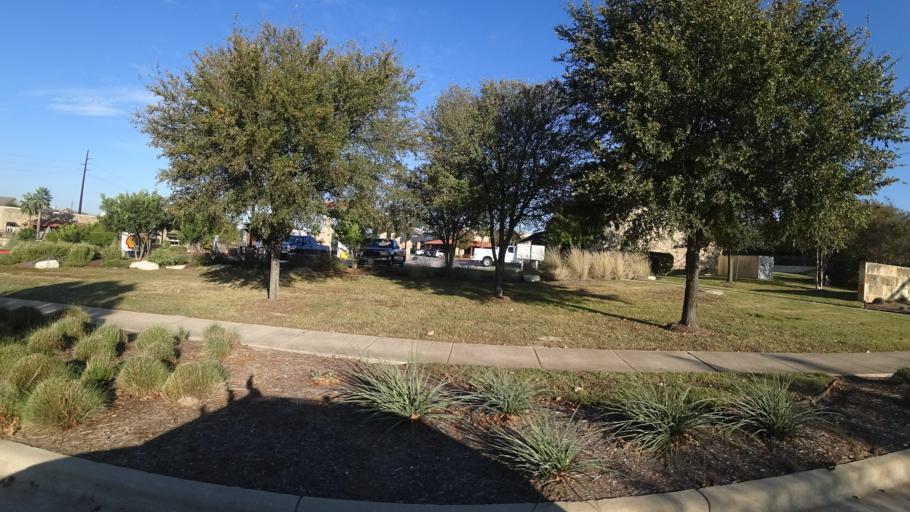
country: US
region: Texas
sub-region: Travis County
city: Hudson Bend
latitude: 30.3691
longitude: -97.8922
